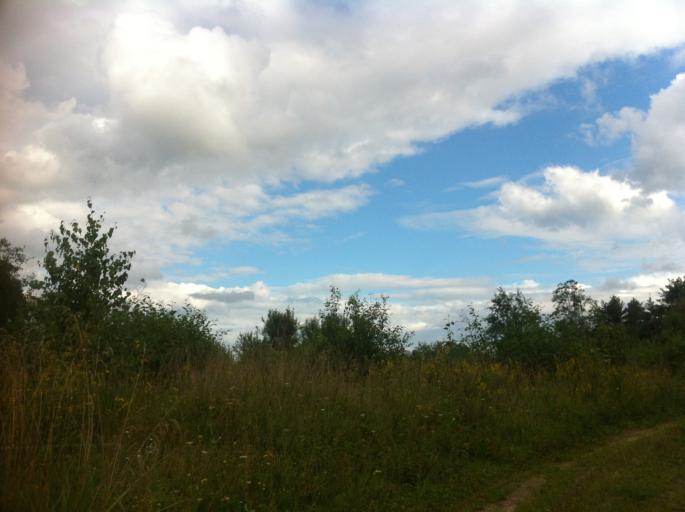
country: RU
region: Pskov
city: Izborsk
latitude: 57.8208
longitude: 27.9686
